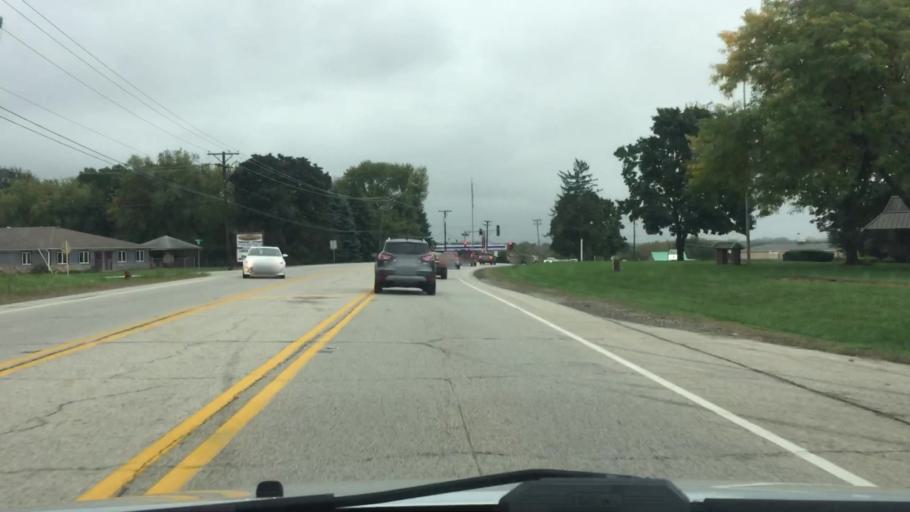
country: US
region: Illinois
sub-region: McHenry County
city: McCullom Lake
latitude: 42.3801
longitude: -88.2710
